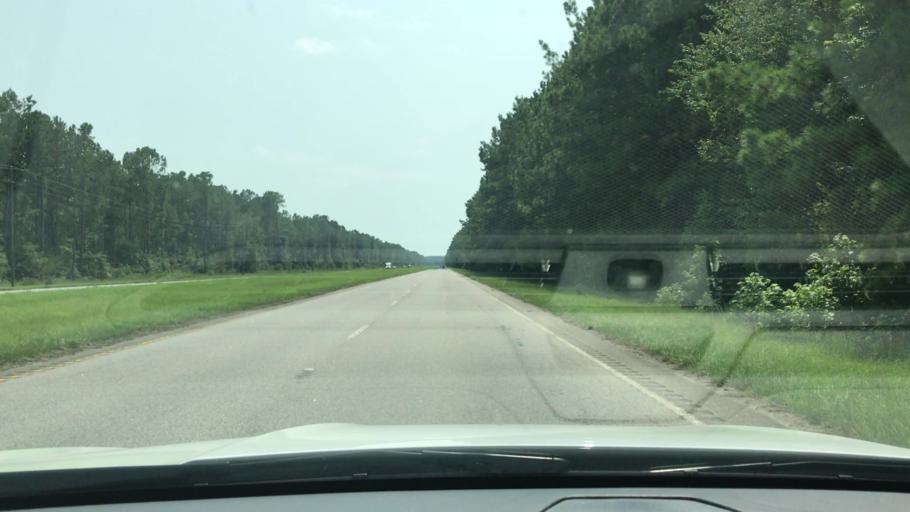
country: US
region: South Carolina
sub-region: Charleston County
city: Awendaw
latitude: 33.0214
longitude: -79.6319
